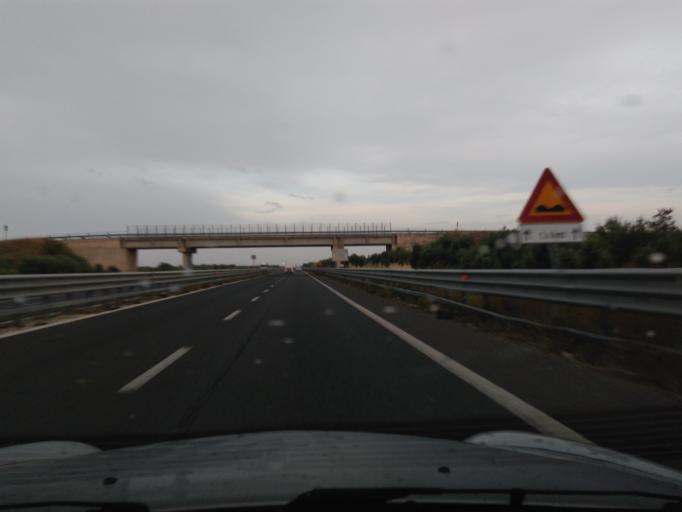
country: IT
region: Apulia
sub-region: Provincia di Bari
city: Giovinazzo
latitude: 41.1649
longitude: 16.7104
